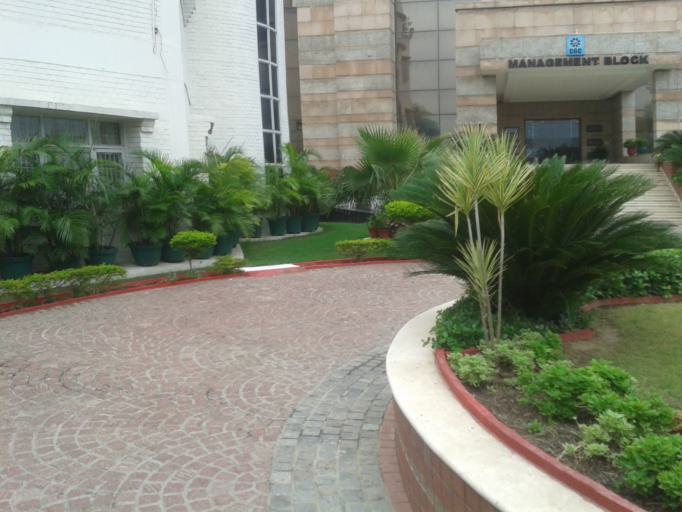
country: IN
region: Punjab
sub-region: Ajitgarh
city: Mohali
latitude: 30.6877
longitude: 76.6645
